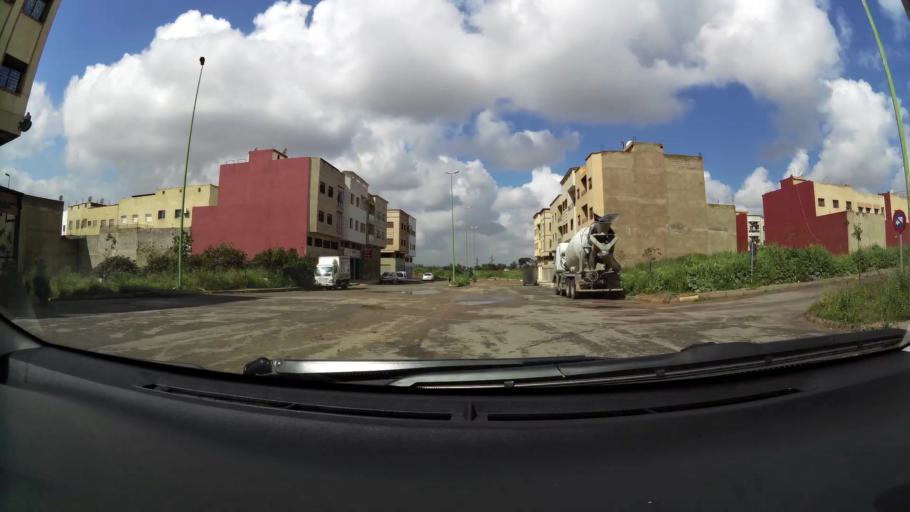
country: MA
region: Grand Casablanca
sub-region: Mediouna
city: Tit Mellil
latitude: 33.5468
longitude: -7.4901
